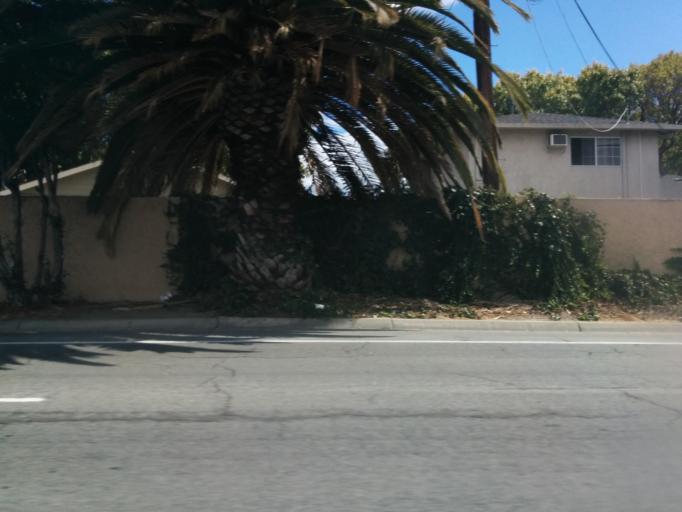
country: US
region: California
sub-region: Santa Clara County
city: Sunnyvale
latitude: 37.3625
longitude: -121.9960
